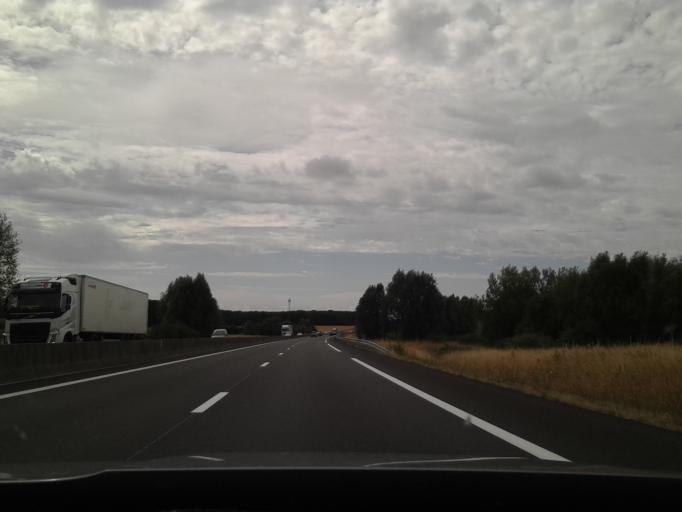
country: FR
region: Pays de la Loire
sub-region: Departement de la Sarthe
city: Beaumont-sur-Sarthe
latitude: 48.3014
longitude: 0.1499
